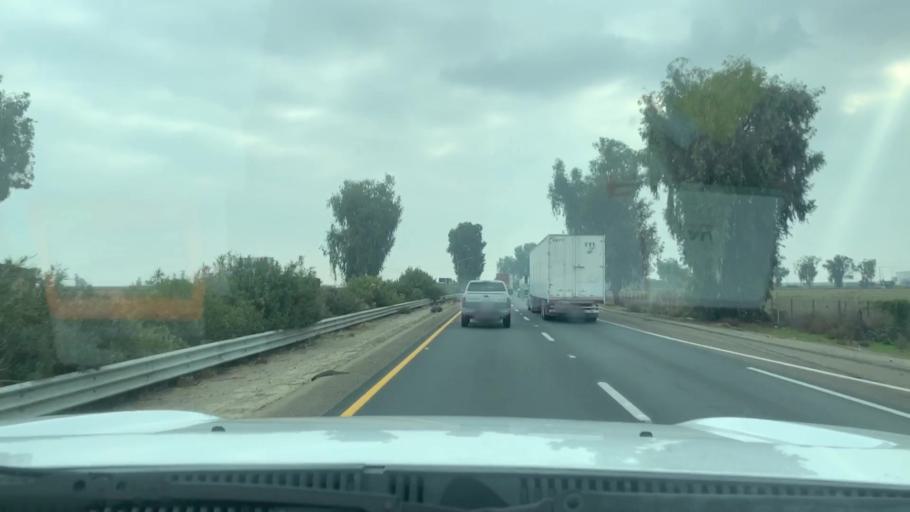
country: US
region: California
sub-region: Tulare County
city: Tipton
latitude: 36.0556
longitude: -119.3114
